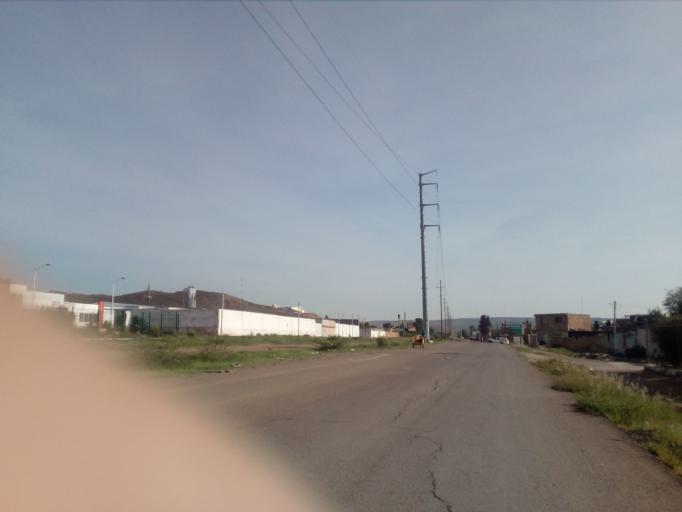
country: MX
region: Durango
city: Victoria de Durango
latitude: 24.0522
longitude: -104.6553
